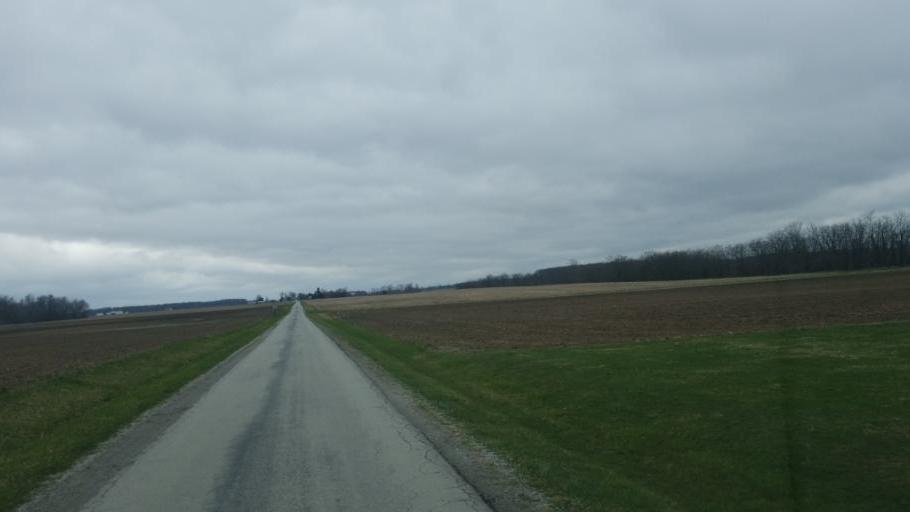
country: US
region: Ohio
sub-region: Hardin County
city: Forest
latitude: 40.7234
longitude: -83.4845
